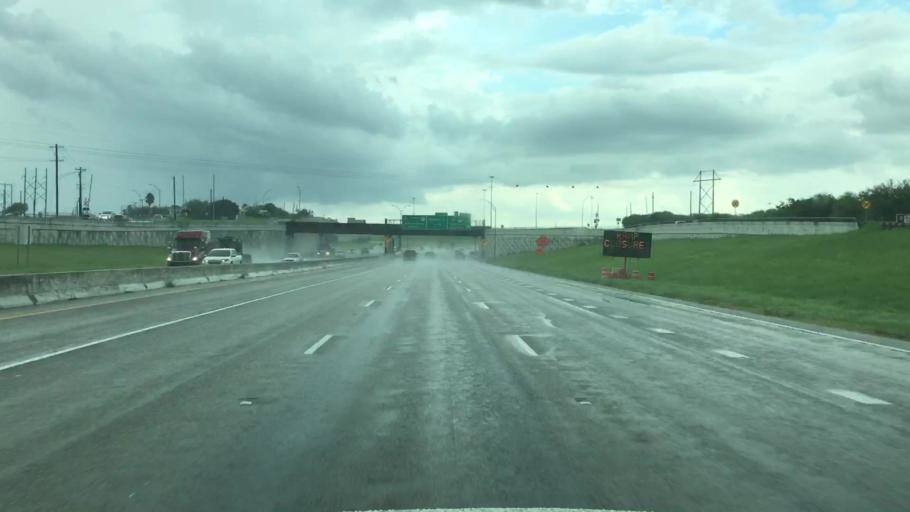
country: US
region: Texas
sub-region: Nueces County
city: Robstown
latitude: 27.8613
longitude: -97.6146
